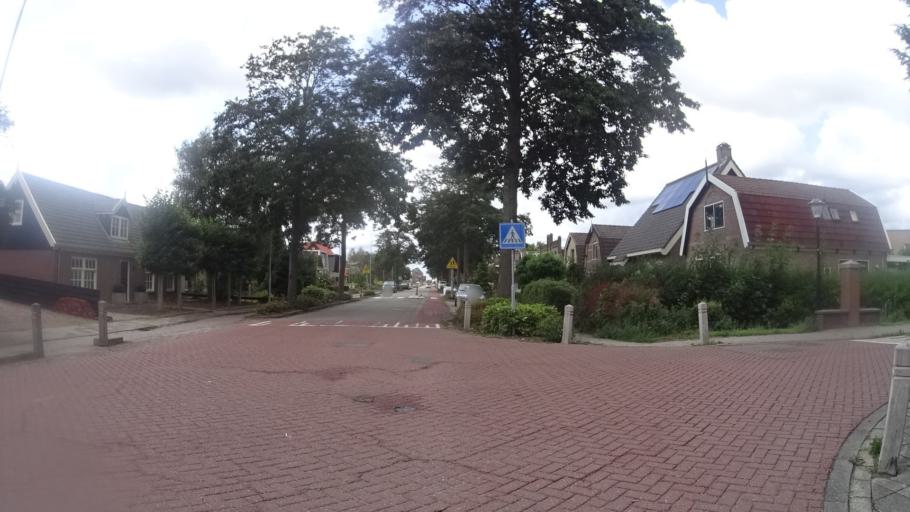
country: NL
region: North Holland
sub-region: Gemeente Schagen
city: Schagen
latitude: 52.8006
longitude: 4.7636
